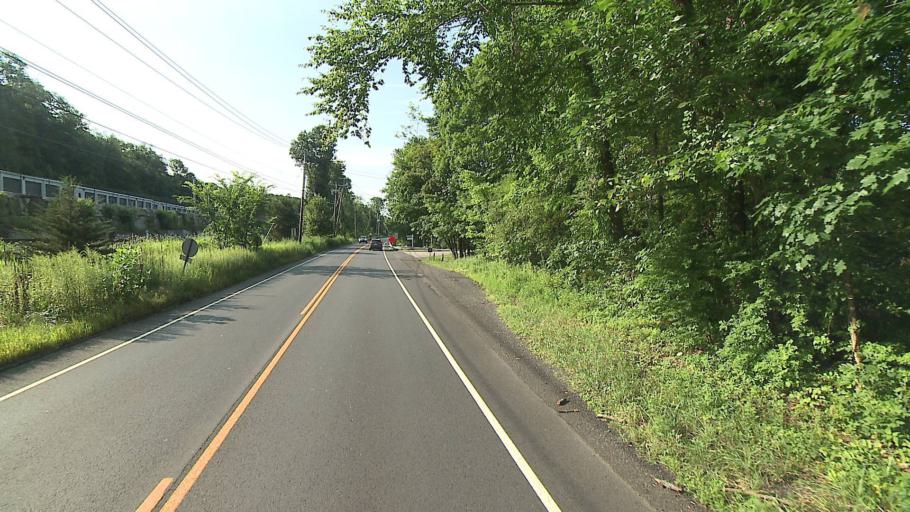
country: US
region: Connecticut
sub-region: Fairfield County
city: Georgetown
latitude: 41.2707
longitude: -73.4426
